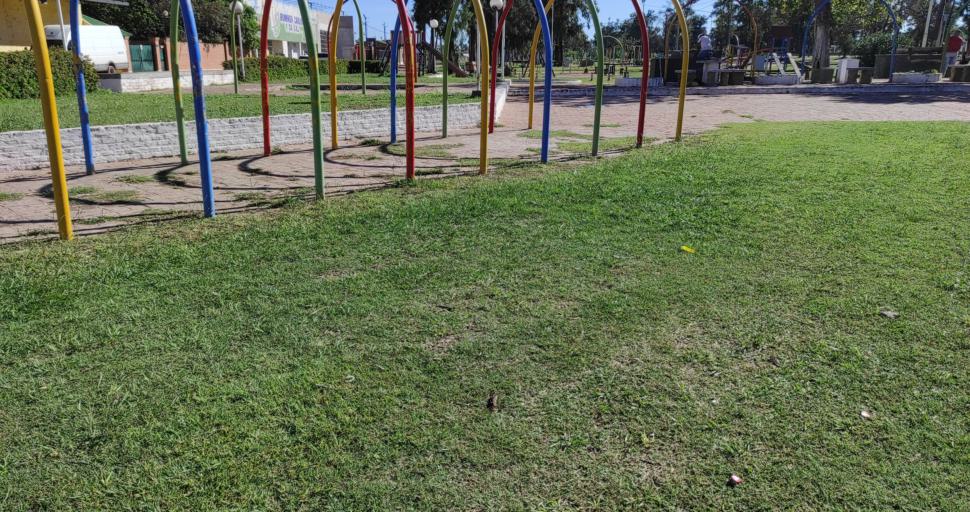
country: AR
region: Chaco
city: Charata
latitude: -27.2258
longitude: -61.1778
